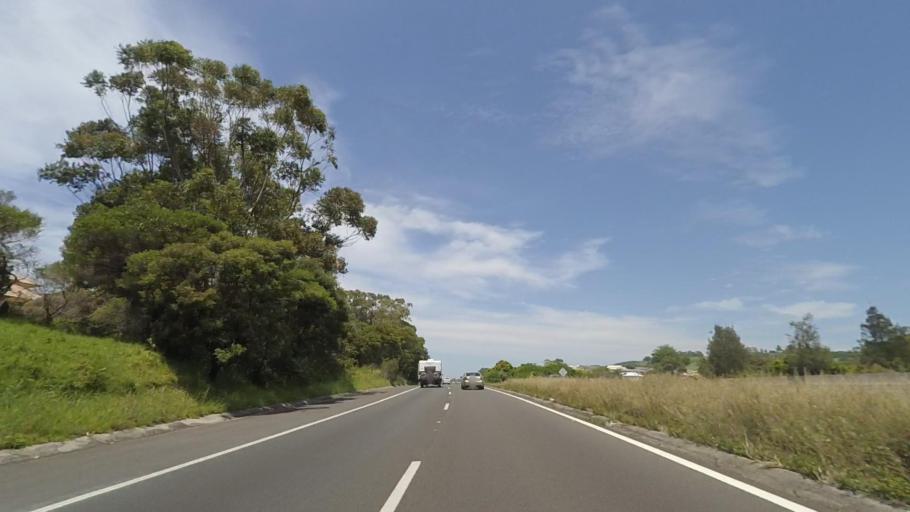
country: AU
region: New South Wales
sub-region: Kiama
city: Kiama
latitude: -34.6736
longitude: 150.8428
